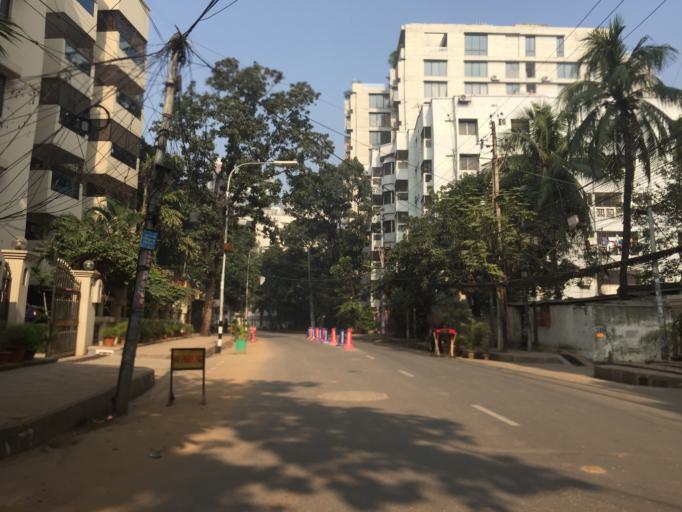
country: BD
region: Dhaka
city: Paltan
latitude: 23.7932
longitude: 90.4201
